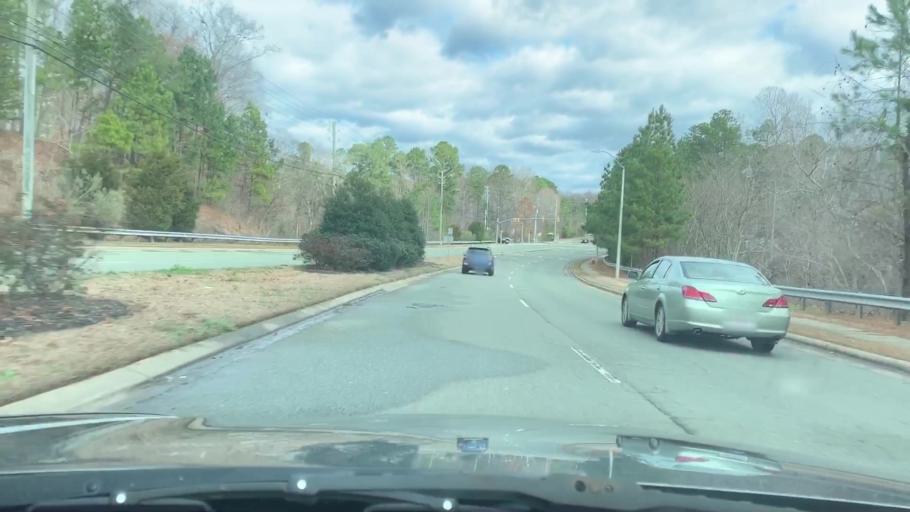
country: US
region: North Carolina
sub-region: Wake County
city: Cary
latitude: 35.8083
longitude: -78.7823
